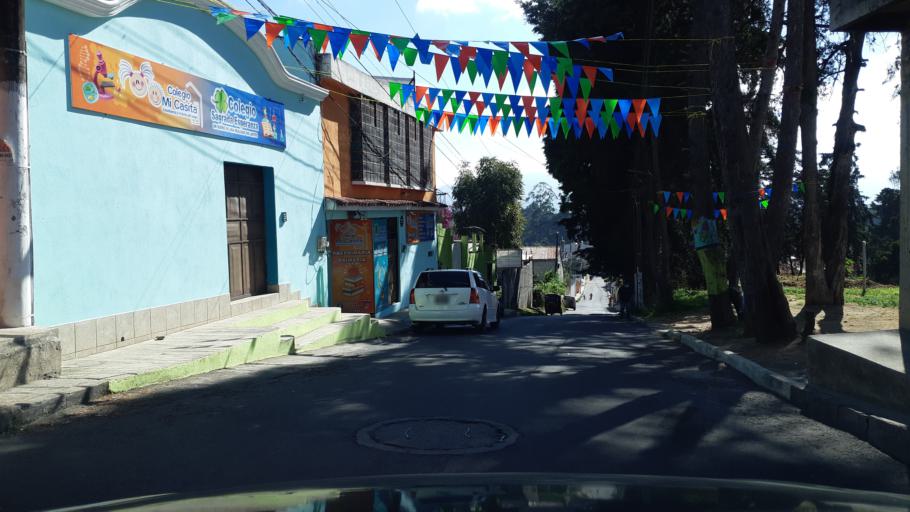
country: GT
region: Chimaltenango
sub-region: Municipio de Chimaltenango
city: Chimaltenango
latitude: 14.6554
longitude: -90.8186
